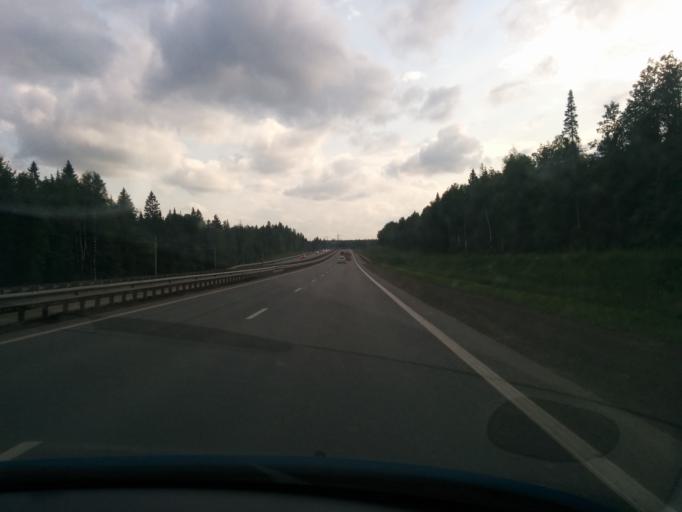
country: RU
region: Perm
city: Ferma
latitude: 58.0226
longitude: 56.4210
